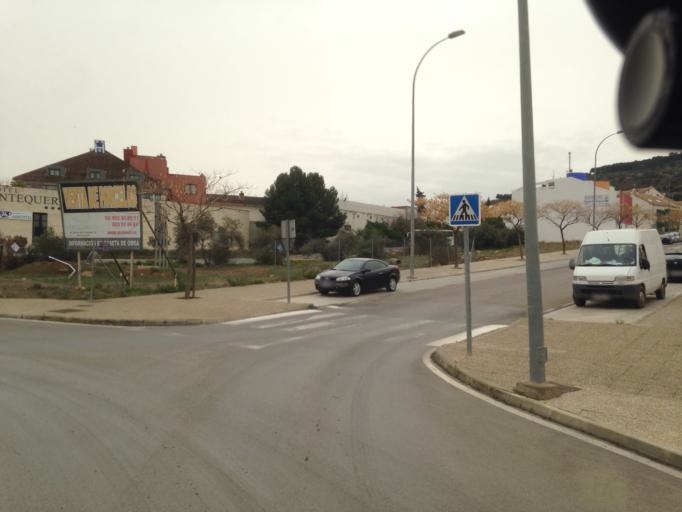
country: ES
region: Andalusia
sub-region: Provincia de Malaga
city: Antequera
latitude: 37.0208
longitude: -4.5759
